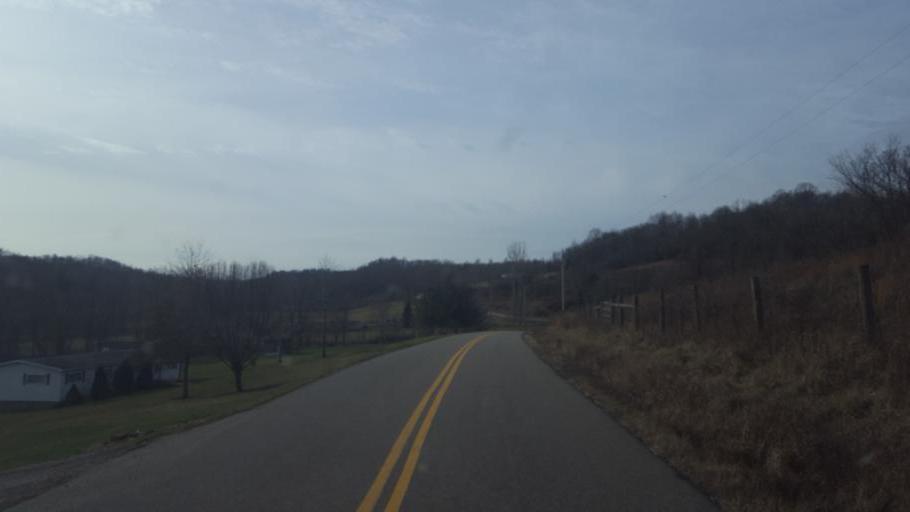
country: US
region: Ohio
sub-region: Gallia County
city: Gallipolis
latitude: 38.7242
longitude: -82.3236
